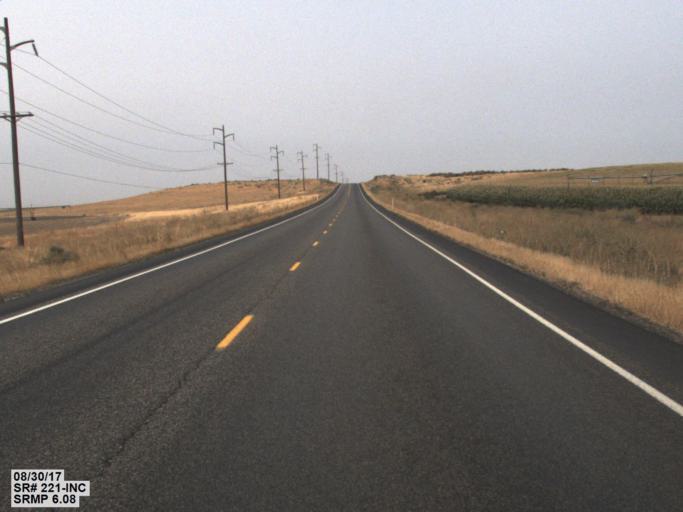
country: US
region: Oregon
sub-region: Morrow County
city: Irrigon
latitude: 46.0232
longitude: -119.6027
